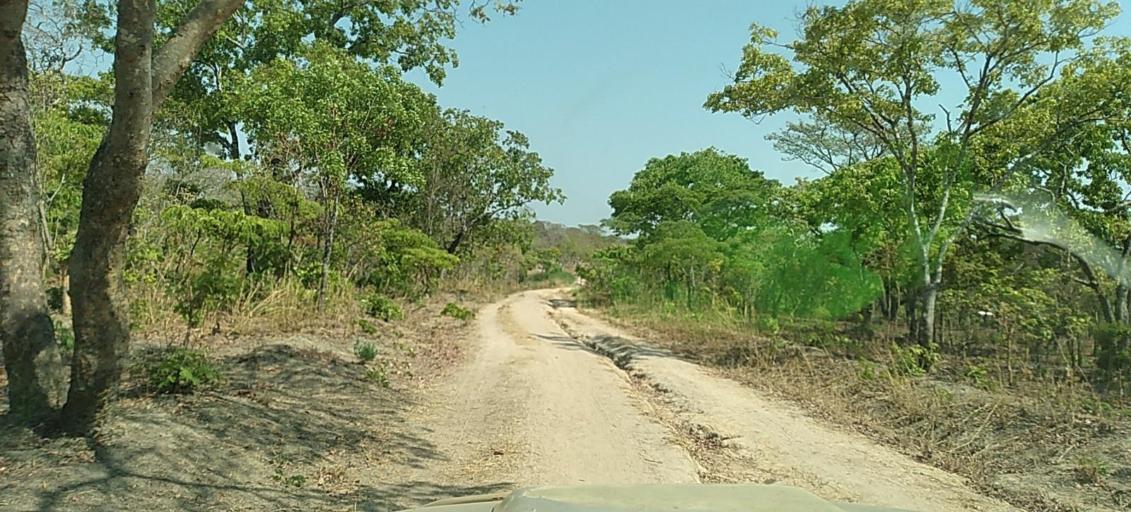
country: ZM
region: North-Western
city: Kalengwa
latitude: -13.3002
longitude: 24.7950
